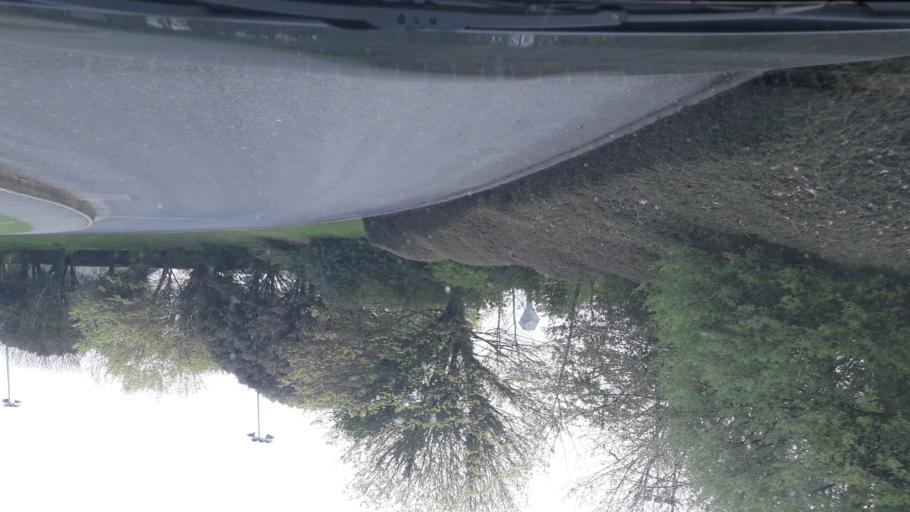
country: IE
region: Leinster
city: Donnybrook
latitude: 53.3061
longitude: -6.2262
